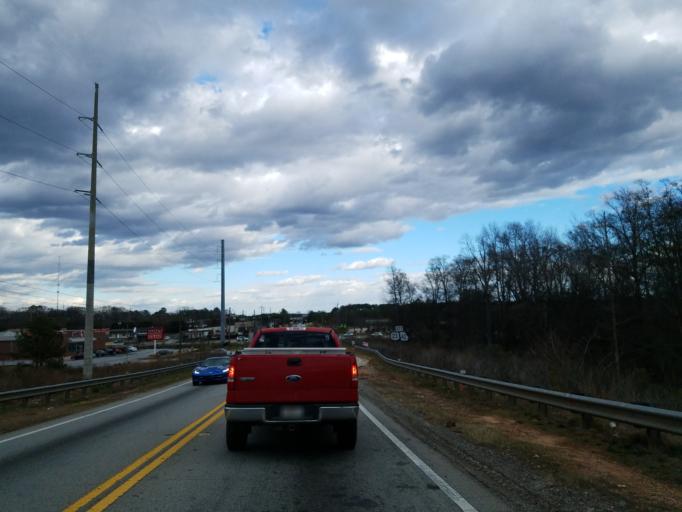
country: US
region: Georgia
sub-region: Henry County
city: McDonough
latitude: 33.4260
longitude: -84.1462
